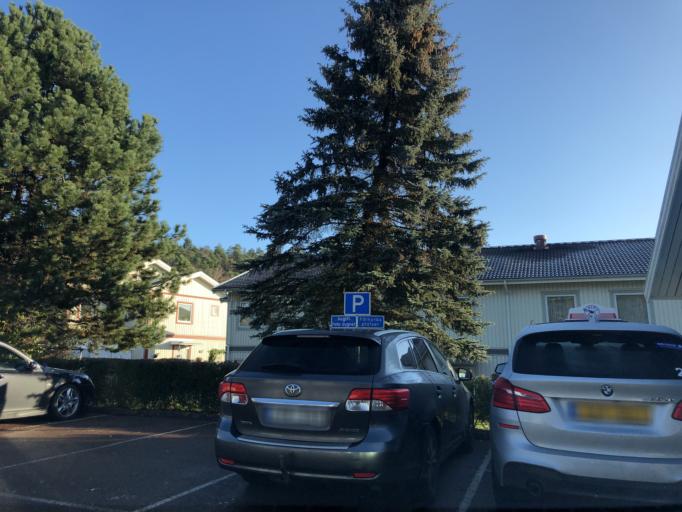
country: SE
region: Vaestra Goetaland
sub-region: Goteborg
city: Rannebergen
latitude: 57.8011
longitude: 12.0531
